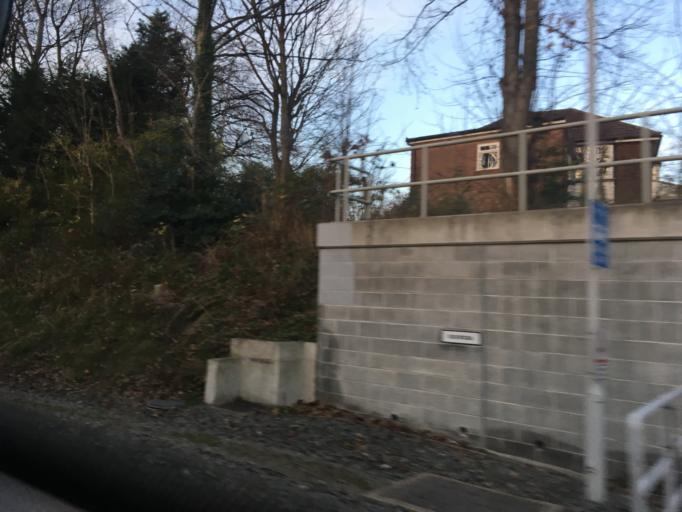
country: GB
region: England
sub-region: Manchester
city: Didsbury
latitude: 53.4294
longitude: -2.2410
